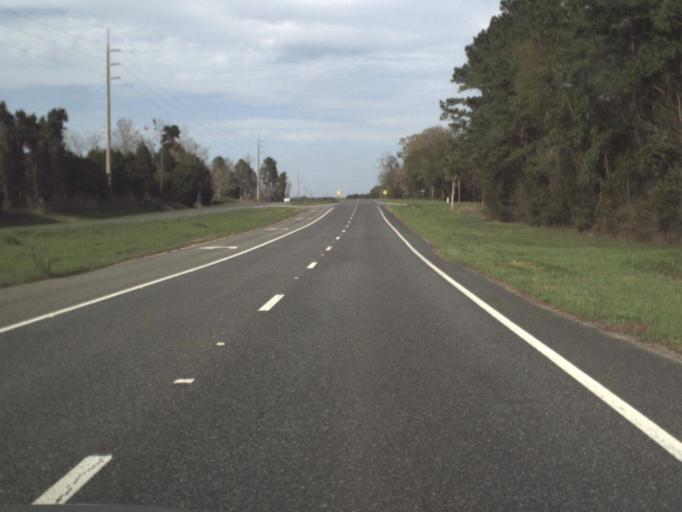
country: US
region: Florida
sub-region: Jefferson County
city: Monticello
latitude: 30.4843
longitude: -83.8851
